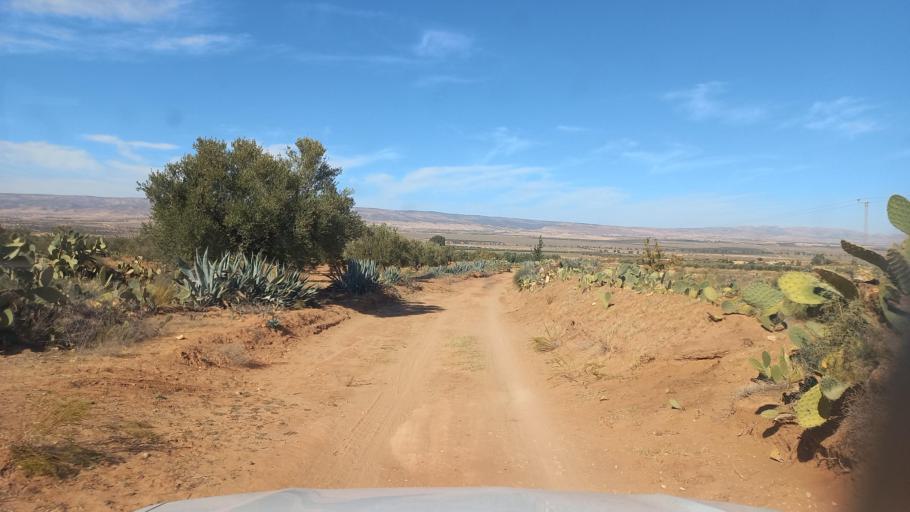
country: TN
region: Al Qasrayn
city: Kasserine
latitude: 35.2023
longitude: 8.9706
